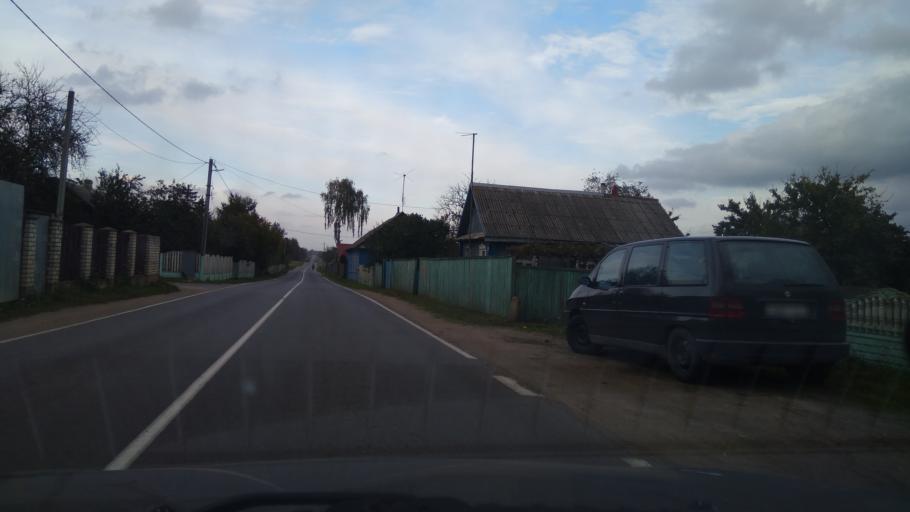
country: BY
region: Minsk
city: Dukora
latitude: 53.6702
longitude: 27.9528
